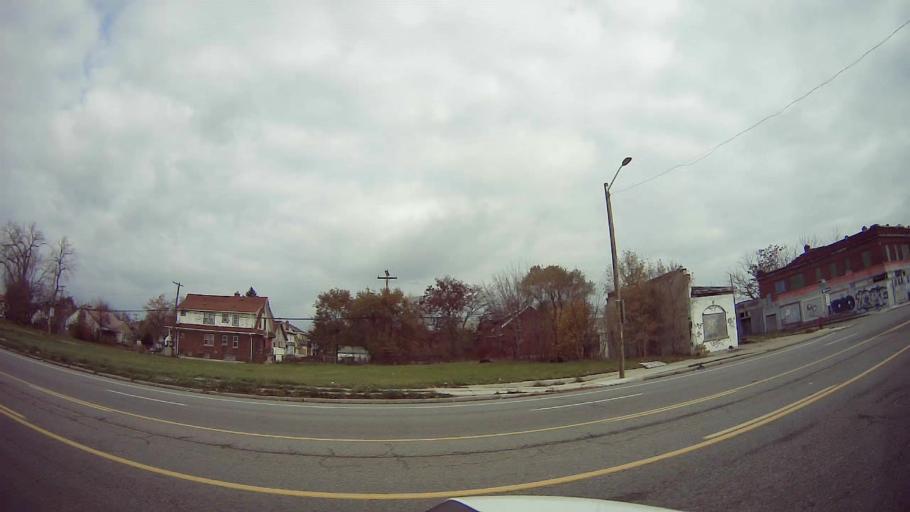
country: US
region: Michigan
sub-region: Wayne County
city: Highland Park
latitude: 42.3854
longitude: -83.1170
